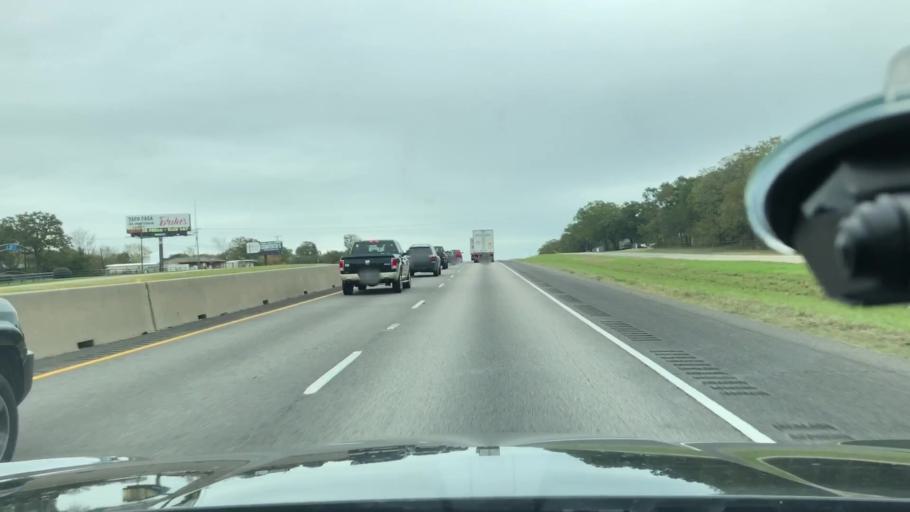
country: US
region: Texas
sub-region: Hopkins County
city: Sulphur Springs
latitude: 33.1471
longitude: -95.5423
